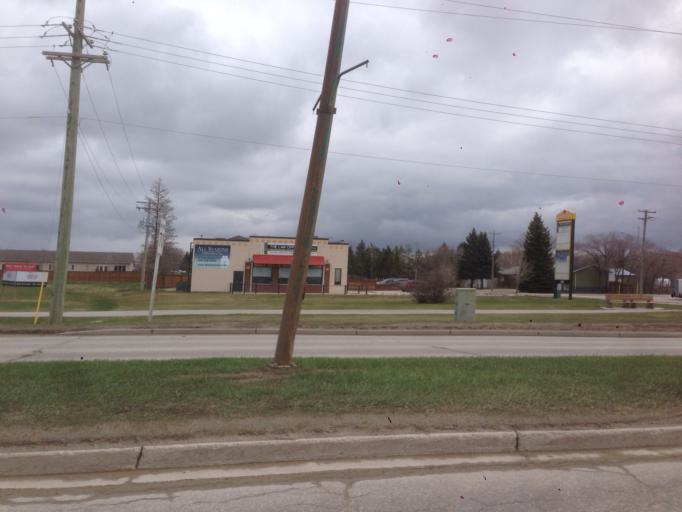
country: CA
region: Manitoba
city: Steinbach
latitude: 49.5352
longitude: -96.6884
